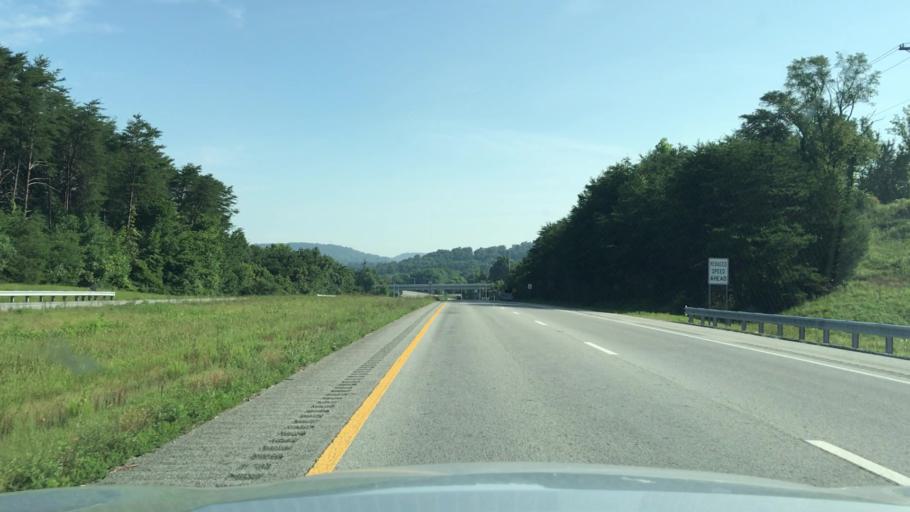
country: US
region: Tennessee
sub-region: Overton County
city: Livingston
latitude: 36.3563
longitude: -85.3428
